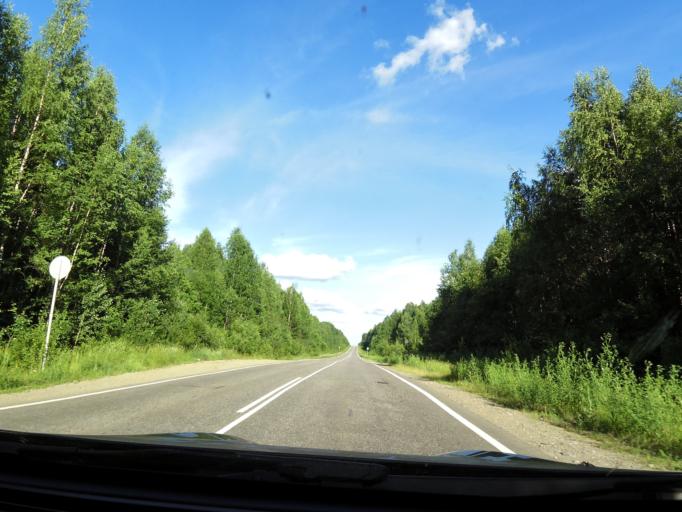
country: RU
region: Kirov
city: Omutninsk
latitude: 58.7641
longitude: 51.9913
